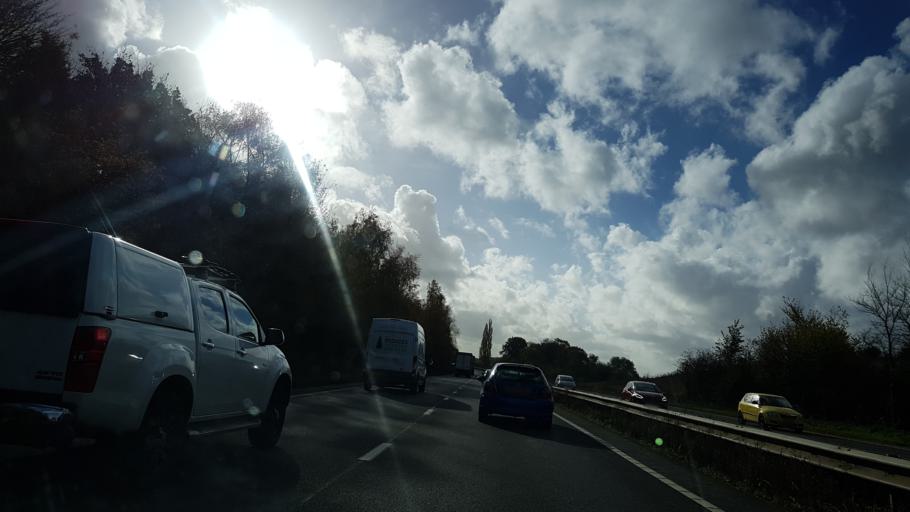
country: GB
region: England
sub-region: Surrey
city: Milford
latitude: 51.2090
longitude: -0.6506
